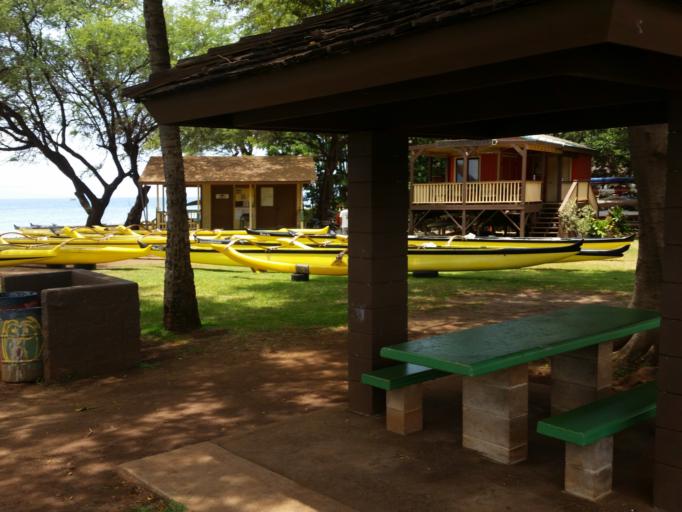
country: US
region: Hawaii
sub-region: Maui County
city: Ka'anapali
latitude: 20.9111
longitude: -156.6898
